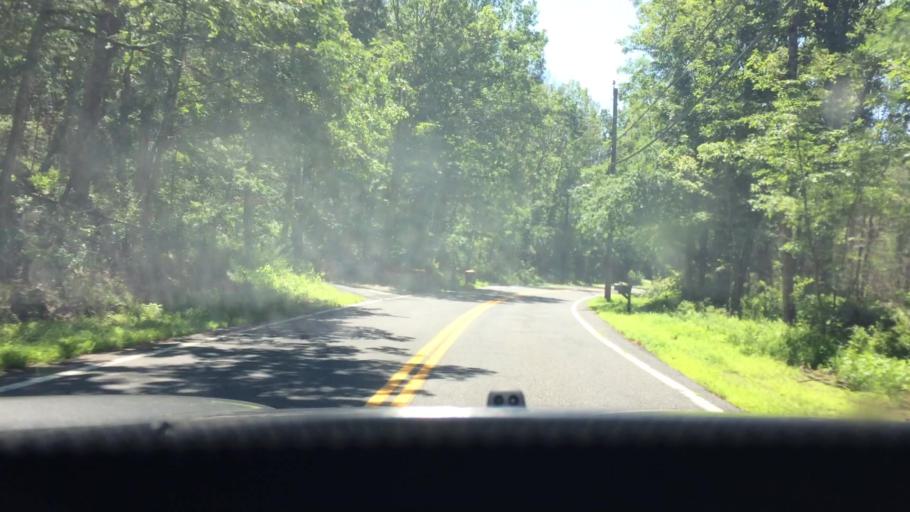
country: US
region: Rhode Island
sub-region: Providence County
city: Harrisville
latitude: 42.0025
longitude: -71.6811
